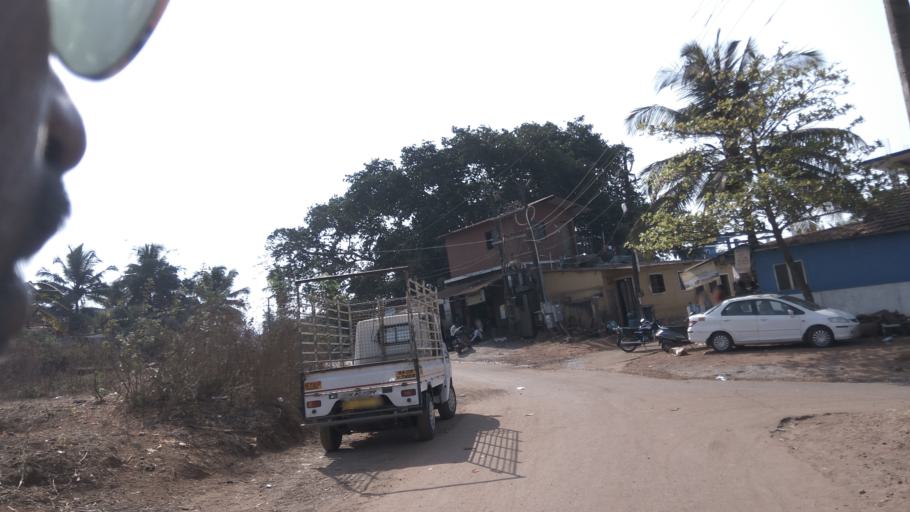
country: IN
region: Goa
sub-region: North Goa
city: Candolim
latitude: 15.5246
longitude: 73.7716
